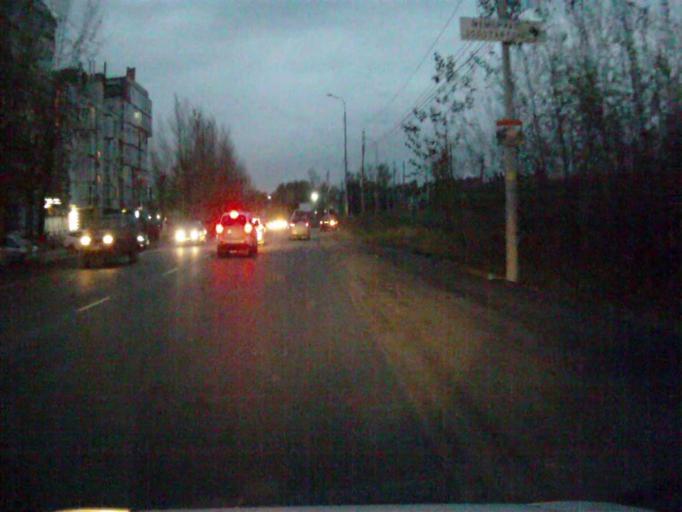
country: RU
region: Chelyabinsk
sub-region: Gorod Chelyabinsk
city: Chelyabinsk
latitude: 55.1589
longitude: 61.2975
